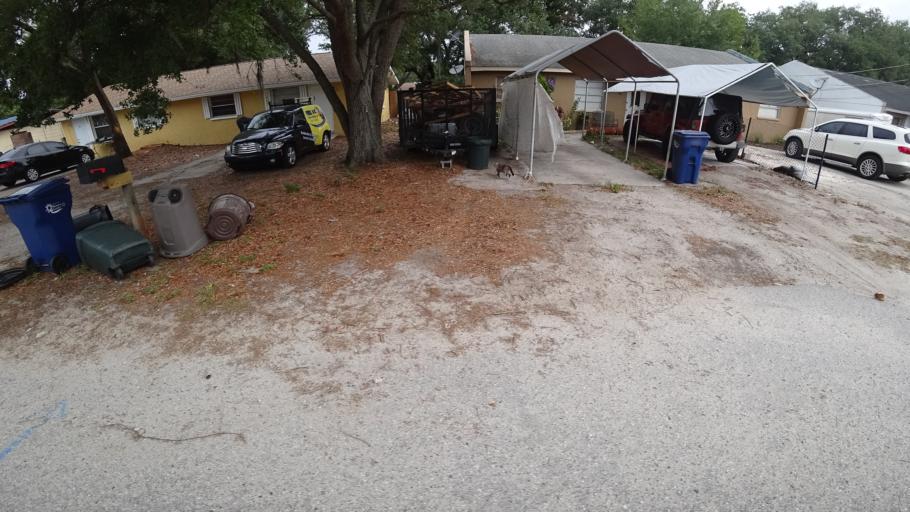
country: US
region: Florida
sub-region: Manatee County
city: West Samoset
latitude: 27.4683
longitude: -82.5535
